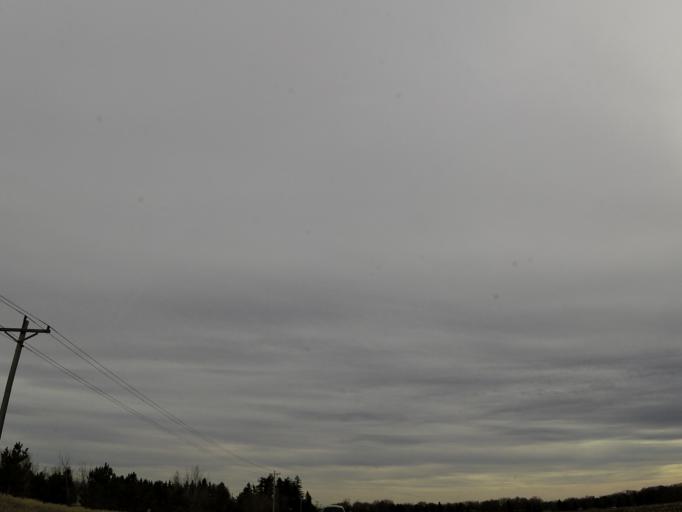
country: US
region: Minnesota
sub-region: Scott County
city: Prior Lake
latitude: 44.7087
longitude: -93.3794
